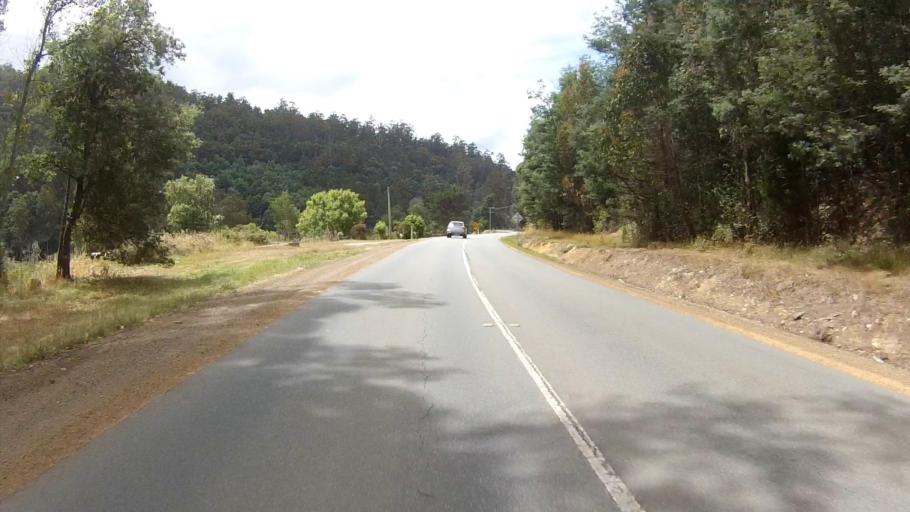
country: AU
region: Tasmania
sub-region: Kingborough
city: Kettering
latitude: -43.1038
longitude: 147.2091
